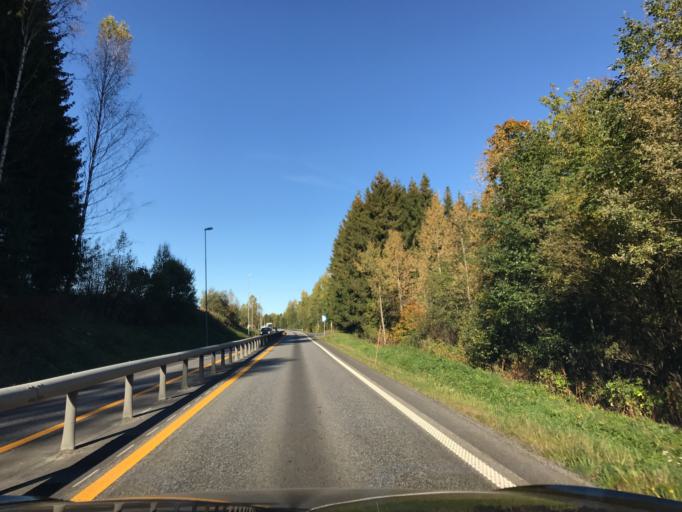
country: NO
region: Oppland
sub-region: Lillehammer
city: Lillehammer
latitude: 61.0092
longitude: 10.4810
